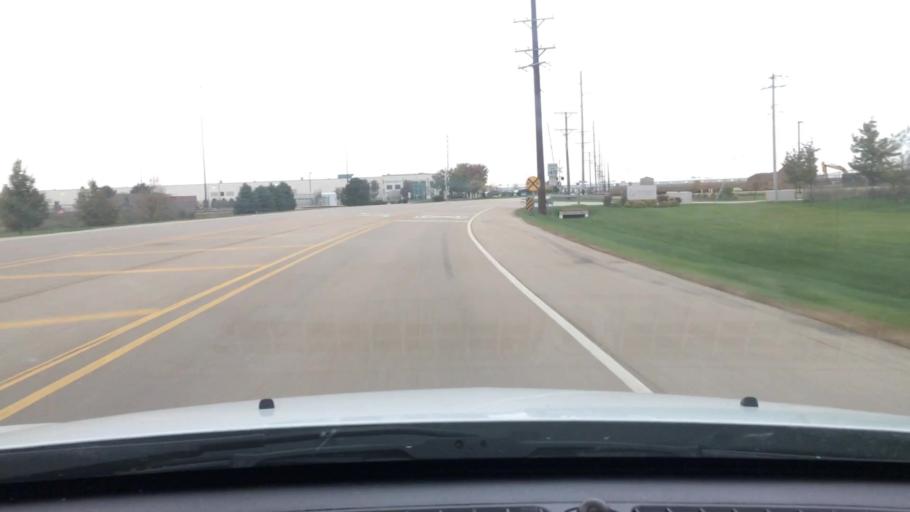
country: US
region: Illinois
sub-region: Ogle County
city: Rochelle
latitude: 41.8912
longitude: -89.0288
